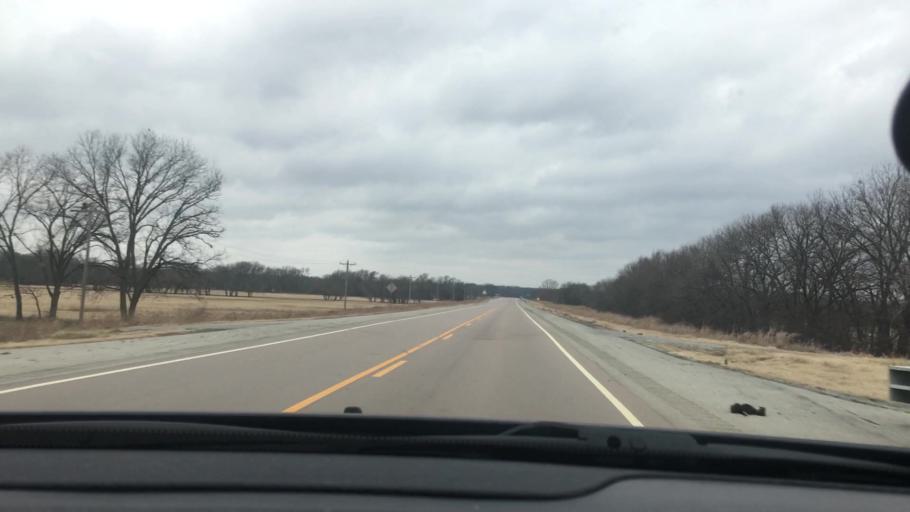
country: US
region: Oklahoma
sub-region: Atoka County
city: Atoka
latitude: 34.3713
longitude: -96.3149
